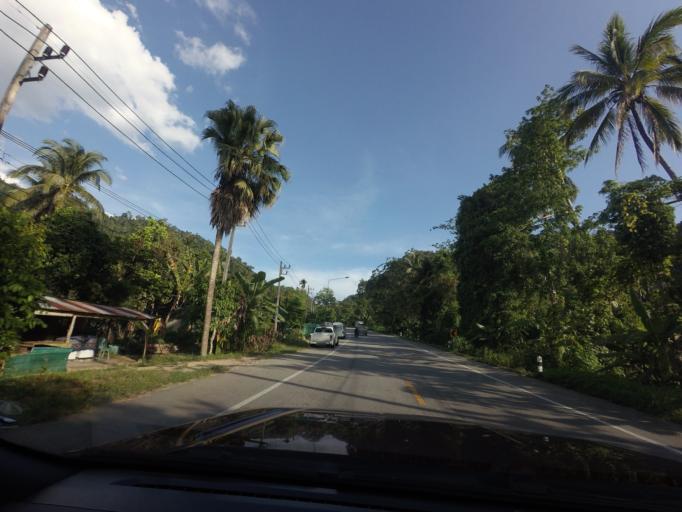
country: TH
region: Yala
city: Than To
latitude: 6.1891
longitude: 101.1726
